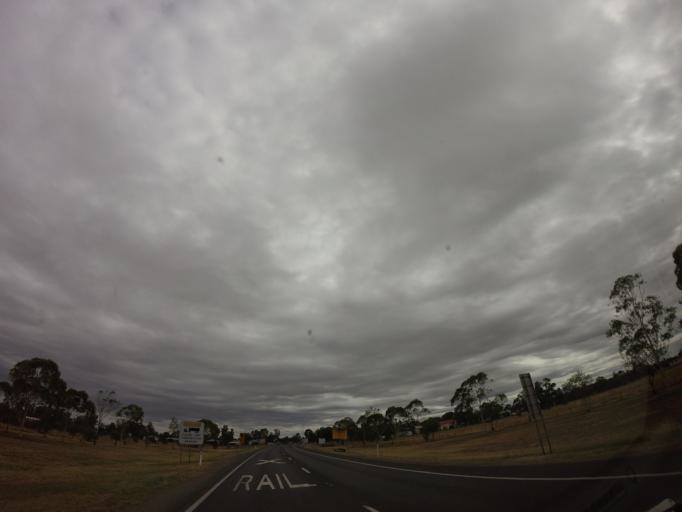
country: AU
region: New South Wales
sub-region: Narrabri
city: Narrabri
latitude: -30.3462
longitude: 149.7608
